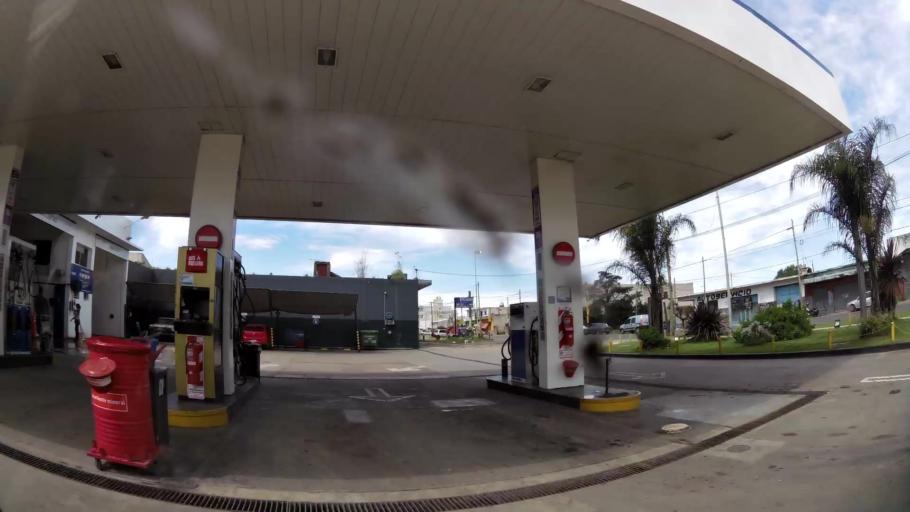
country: AR
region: Buenos Aires
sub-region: Partido de Quilmes
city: Quilmes
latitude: -34.7787
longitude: -58.2898
